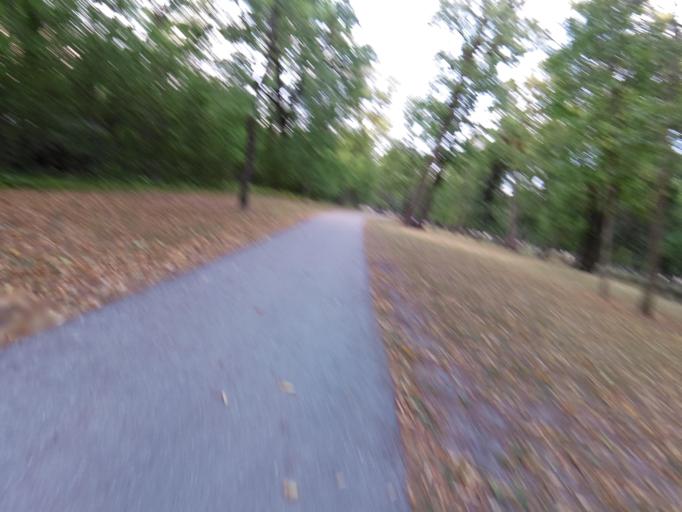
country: CA
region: Manitoba
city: Portage la Prairie
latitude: 49.9627
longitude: -98.2889
